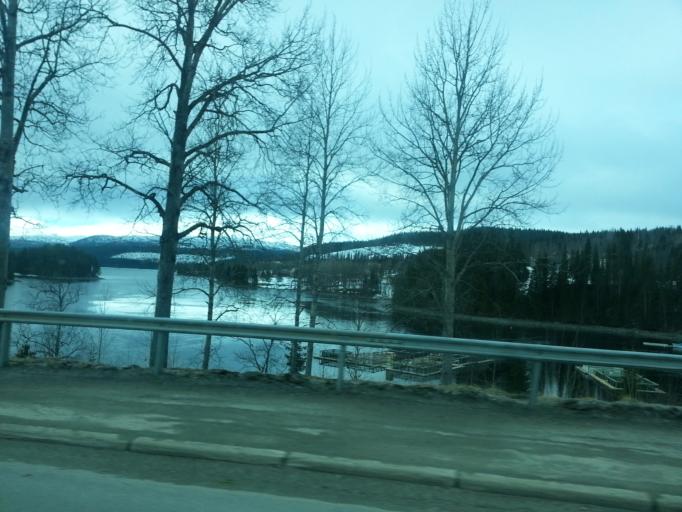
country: NO
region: Nord-Trondelag
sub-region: Lierne
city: Sandvika
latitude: 64.4984
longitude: 14.1459
